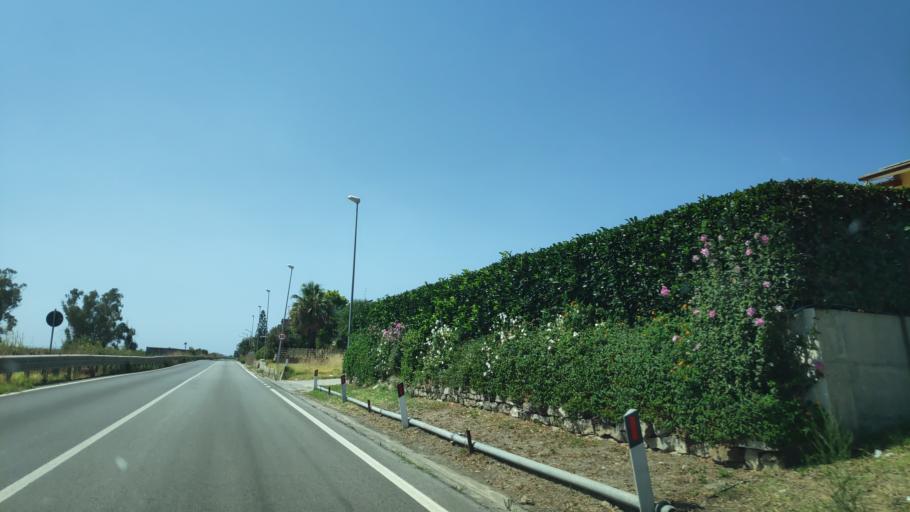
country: IT
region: Calabria
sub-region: Provincia di Reggio Calabria
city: Brancaleone-Marina
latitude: 37.9942
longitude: 16.1215
